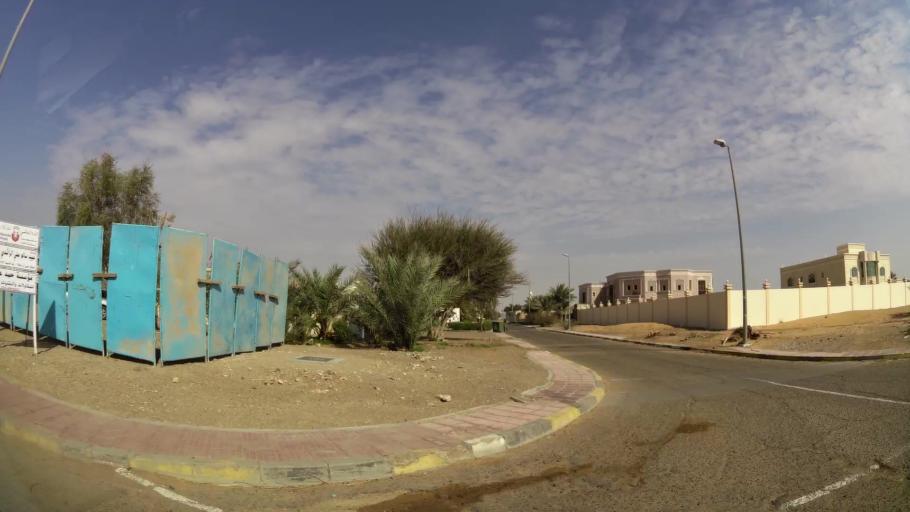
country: AE
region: Abu Dhabi
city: Al Ain
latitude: 24.0976
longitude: 55.9176
